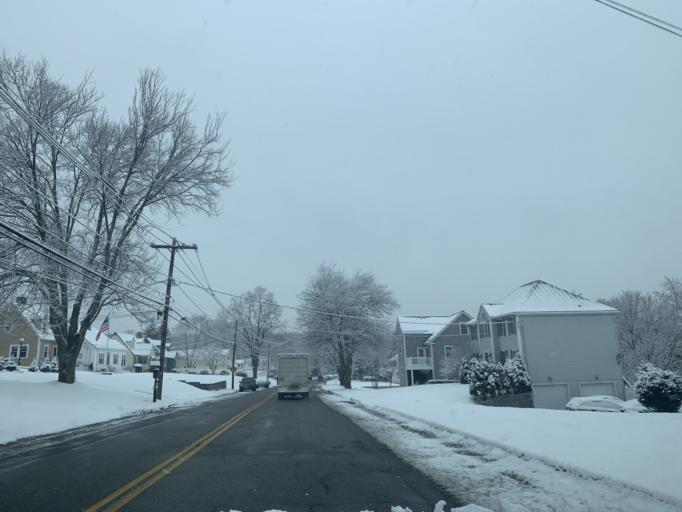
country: US
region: Massachusetts
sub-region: Norfolk County
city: Norwood
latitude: 42.2027
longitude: -71.1916
